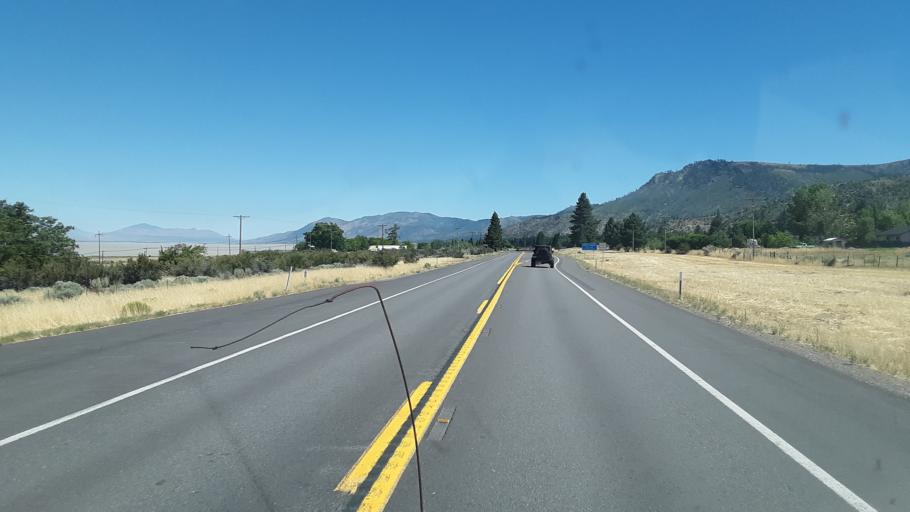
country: US
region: California
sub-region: Lassen County
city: Janesville
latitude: 40.2594
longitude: -120.4687
